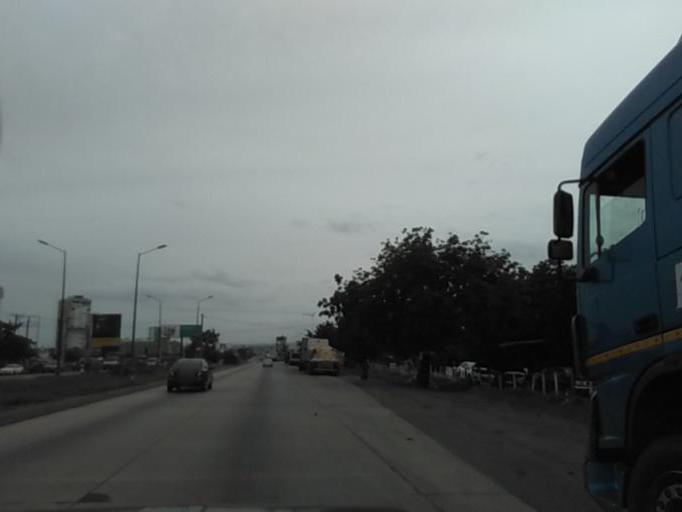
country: GH
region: Greater Accra
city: Medina Estates
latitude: 5.6248
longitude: -0.1714
